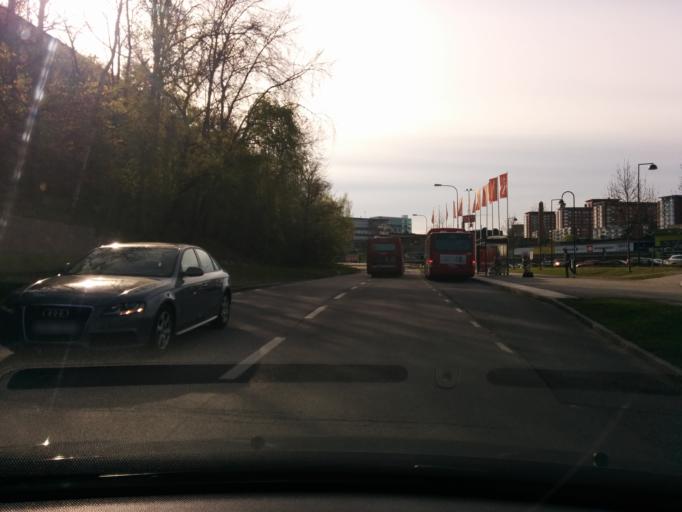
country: SE
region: Stockholm
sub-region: Nacka Kommun
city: Nacka
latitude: 59.3043
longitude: 18.1285
